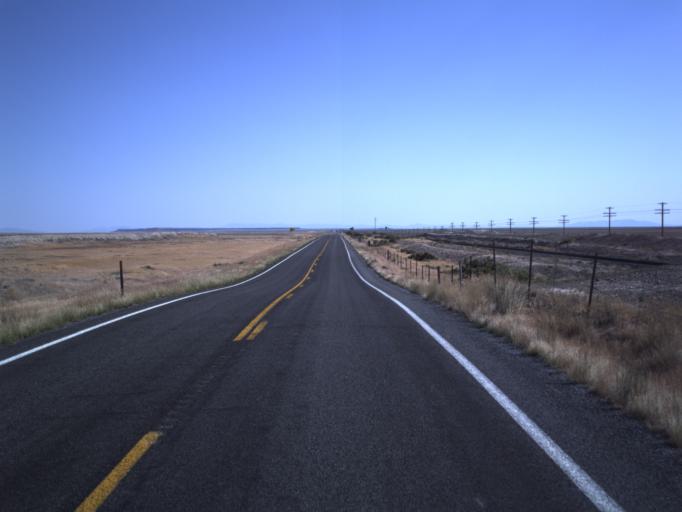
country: US
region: Utah
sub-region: Millard County
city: Delta
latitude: 38.9848
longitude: -112.7936
